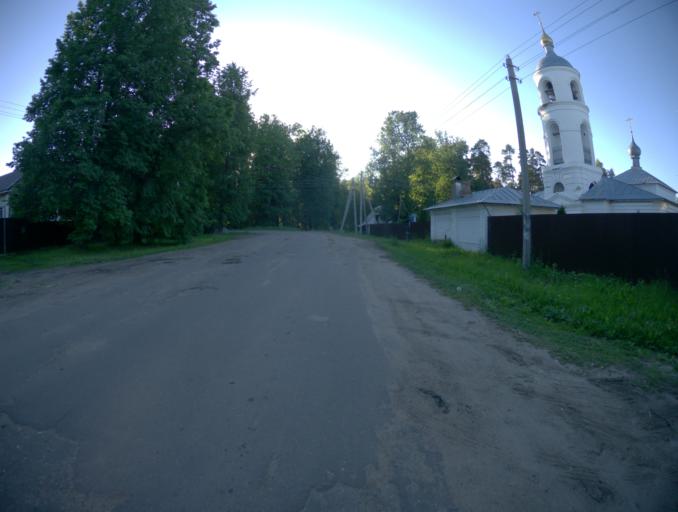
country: RU
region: Ivanovo
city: Lezhnevo
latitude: 56.8647
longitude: 40.7623
